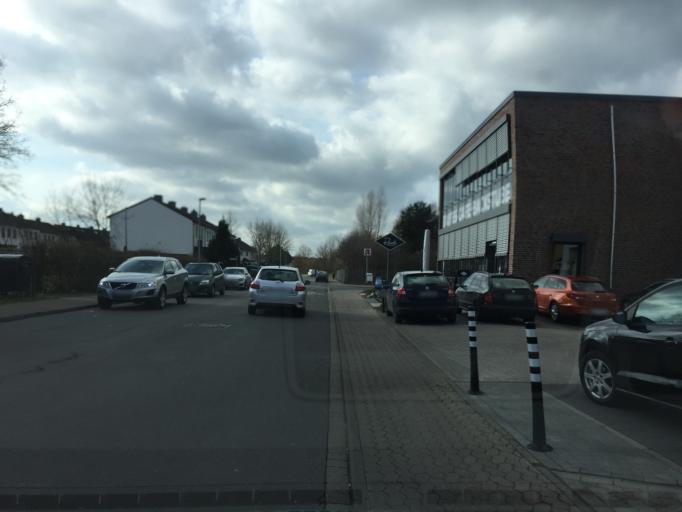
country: DE
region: Lower Saxony
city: Garbsen
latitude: 52.4224
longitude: 9.5836
